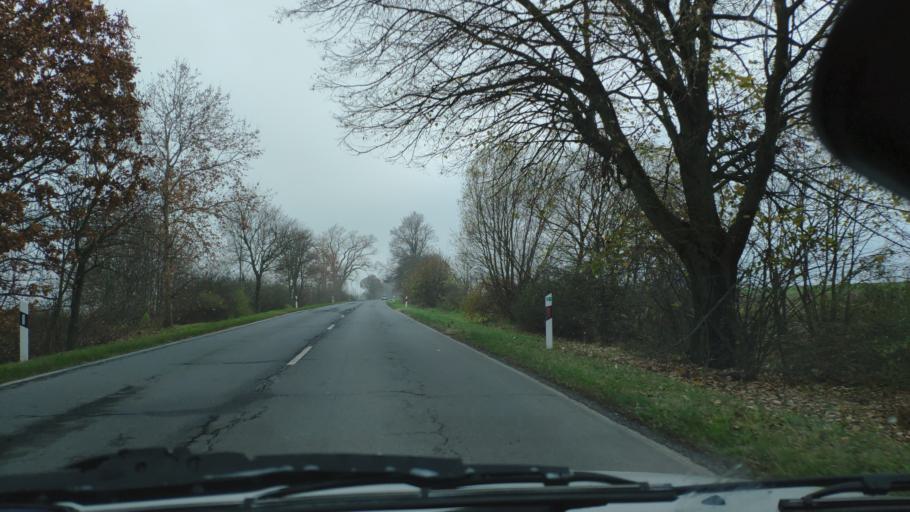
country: HU
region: Zala
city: Zalakomar
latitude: 46.5639
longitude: 17.2614
